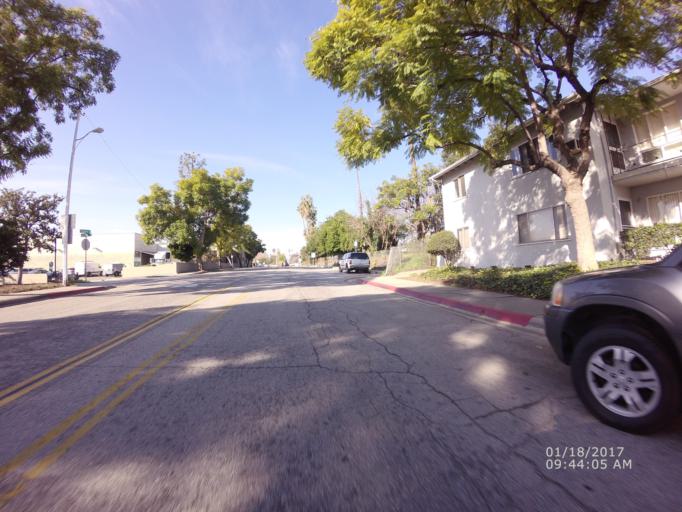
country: US
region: California
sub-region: Los Angeles County
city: South Pasadena
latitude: 34.1190
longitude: -118.1488
